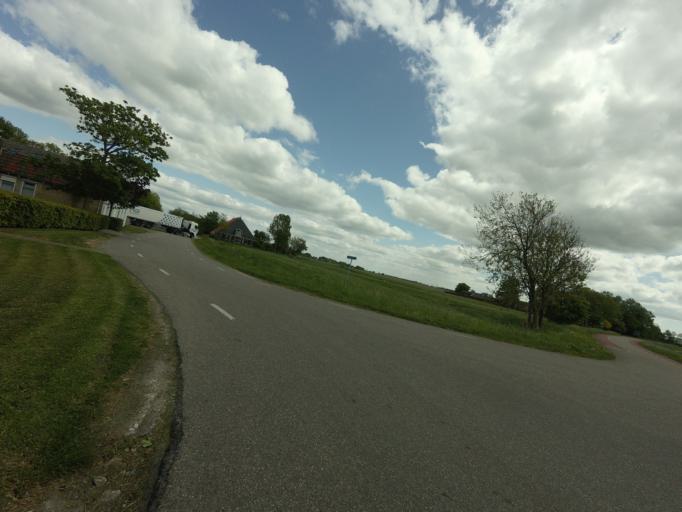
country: NL
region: Friesland
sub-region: Sudwest Fryslan
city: Bolsward
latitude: 53.0926
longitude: 5.5350
